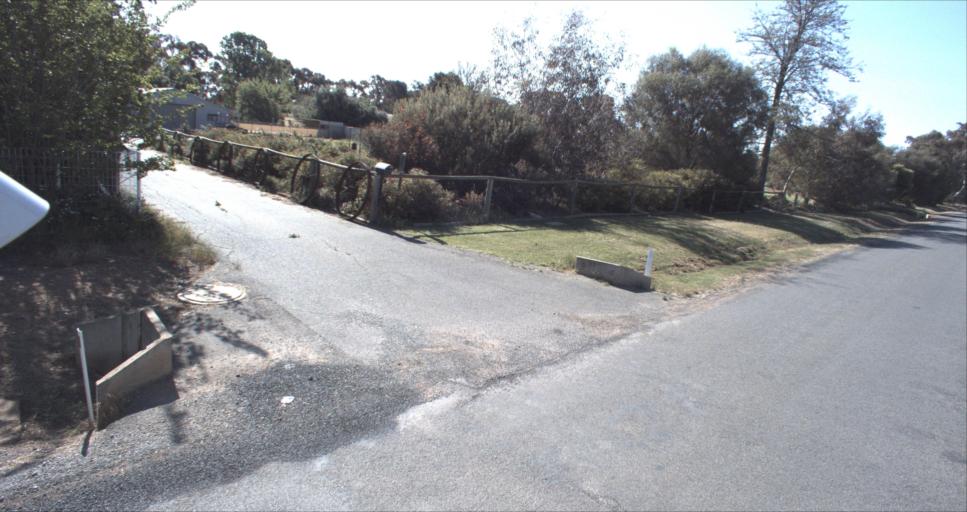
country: AU
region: New South Wales
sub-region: Leeton
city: Leeton
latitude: -34.5711
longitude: 146.4135
